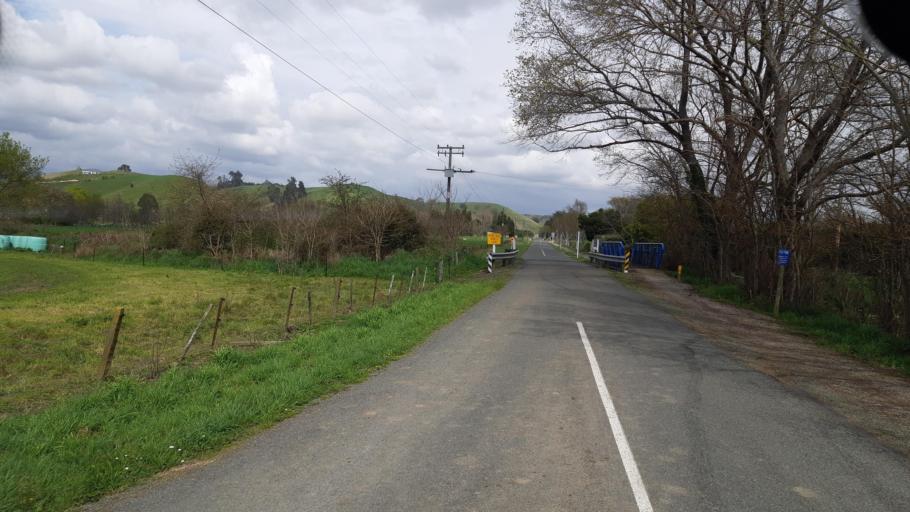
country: NZ
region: Tasman
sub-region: Tasman District
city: Wakefield
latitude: -41.3958
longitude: 173.0747
